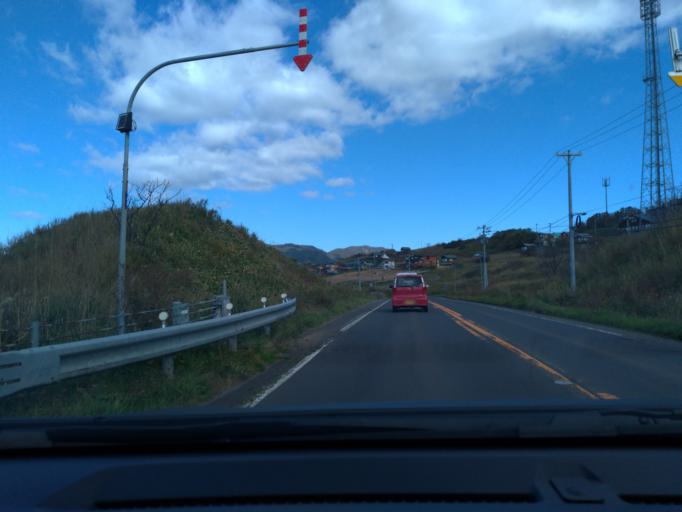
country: JP
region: Hokkaido
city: Ishikari
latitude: 43.3895
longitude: 141.4331
